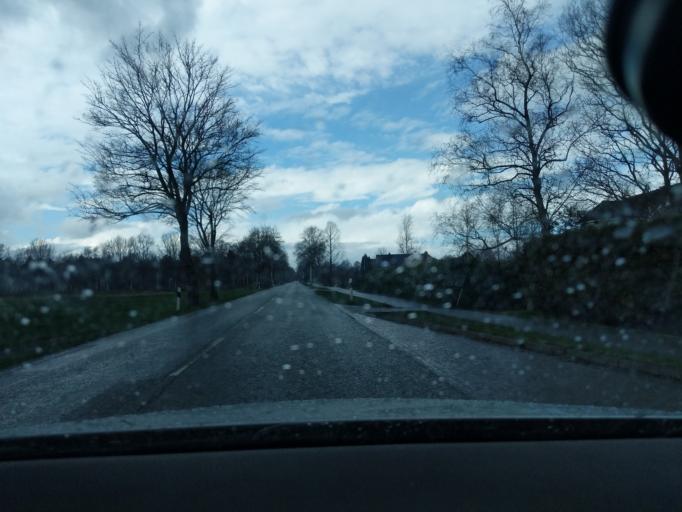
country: DE
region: Lower Saxony
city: Drochtersen
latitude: 53.6623
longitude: 9.4098
